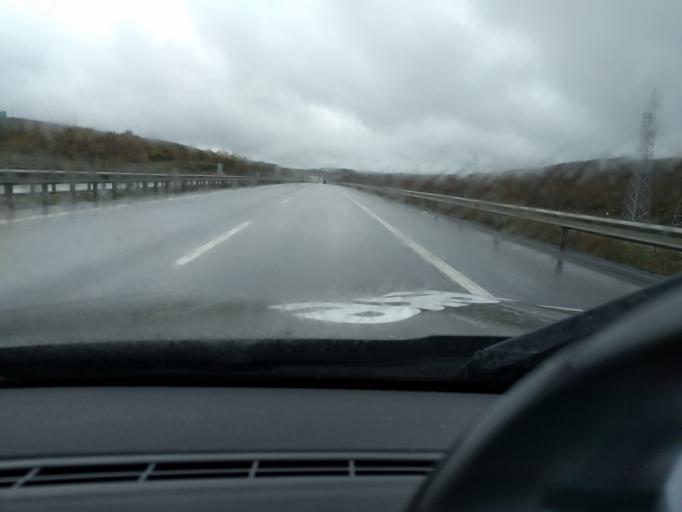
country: TR
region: Istanbul
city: Kemerburgaz
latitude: 41.2238
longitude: 28.8432
